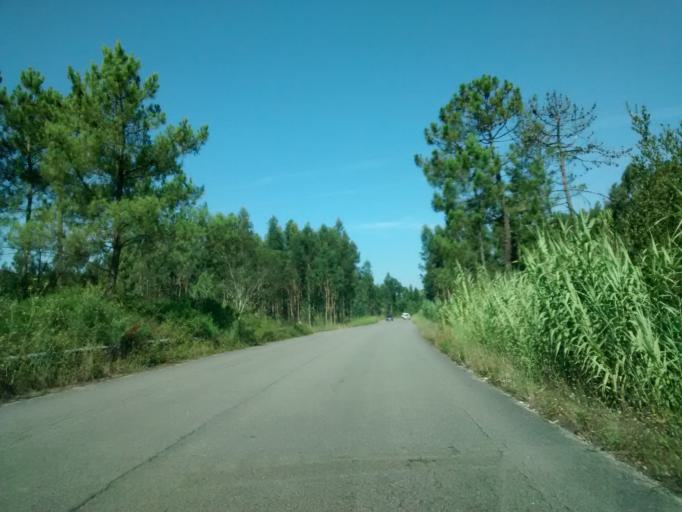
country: PT
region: Coimbra
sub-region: Cantanhede
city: Cantanhede
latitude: 40.4236
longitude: -8.6180
